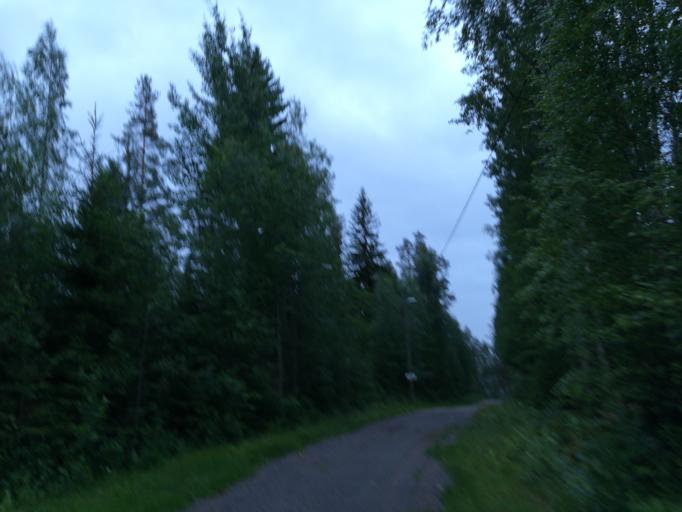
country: FI
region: Southern Savonia
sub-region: Mikkeli
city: Ristiina
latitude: 61.4857
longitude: 27.2814
